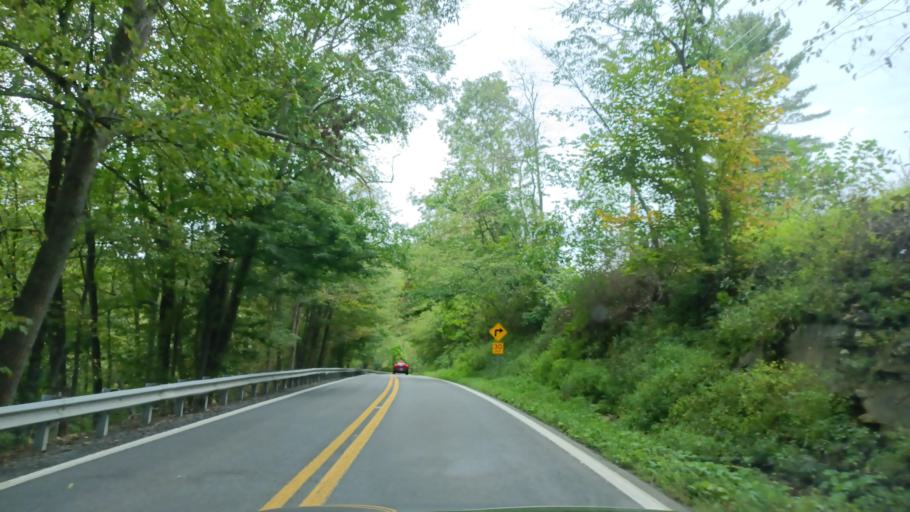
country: US
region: West Virginia
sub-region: Taylor County
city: Grafton
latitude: 39.3347
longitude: -79.8664
